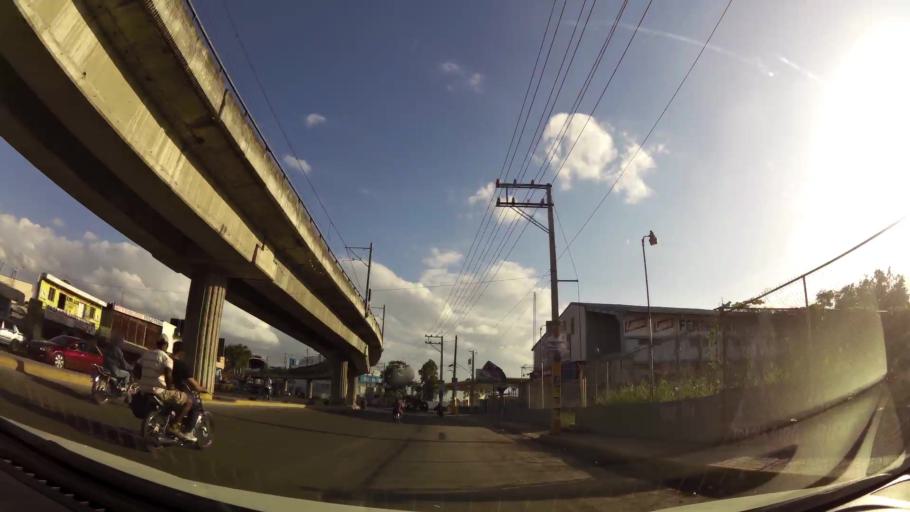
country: DO
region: Nacional
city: Ensanche Luperon
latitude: 18.5486
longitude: -69.9016
